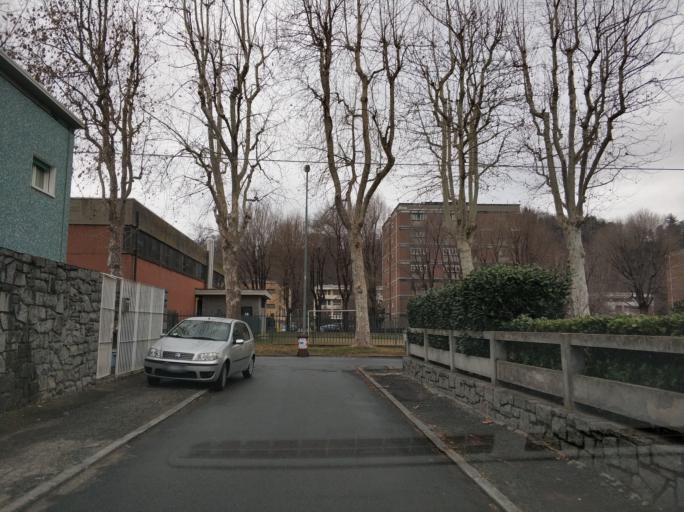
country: IT
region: Piedmont
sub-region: Provincia di Torino
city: Ivrea
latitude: 45.4501
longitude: 7.8778
